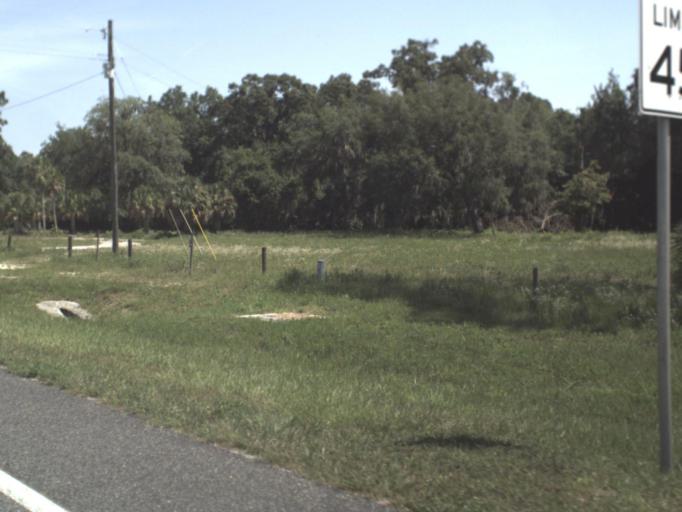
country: US
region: Florida
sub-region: Levy County
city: Manatee Road
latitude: 29.5819
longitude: -82.9193
